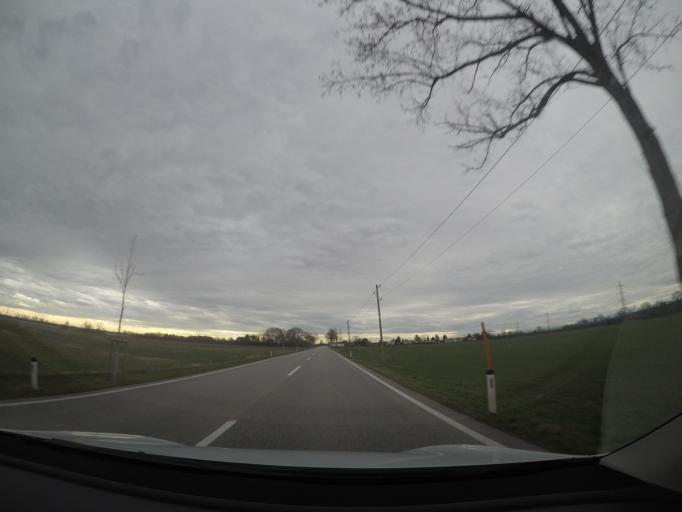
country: AT
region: Lower Austria
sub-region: Politischer Bezirk Modling
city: Achau
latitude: 48.0638
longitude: 16.3821
